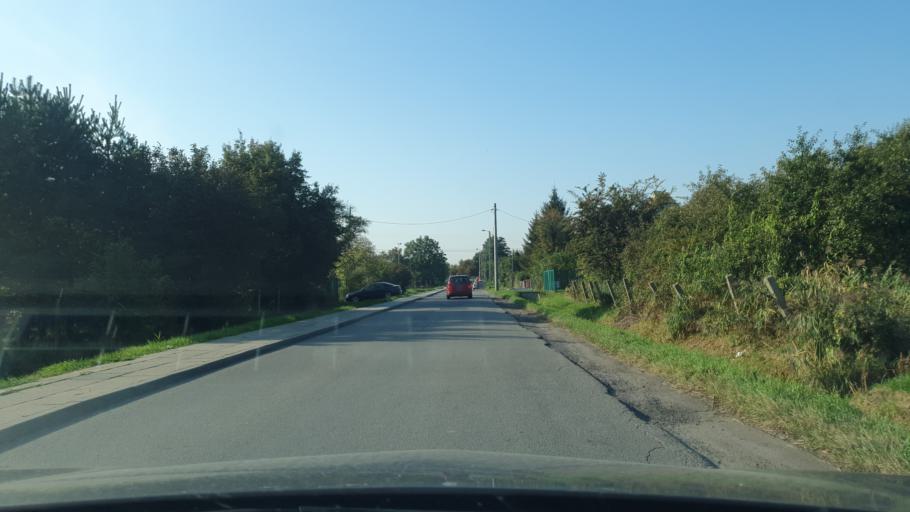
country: PL
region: Pomeranian Voivodeship
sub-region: Gdansk
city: Gdansk
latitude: 54.3475
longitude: 18.6821
